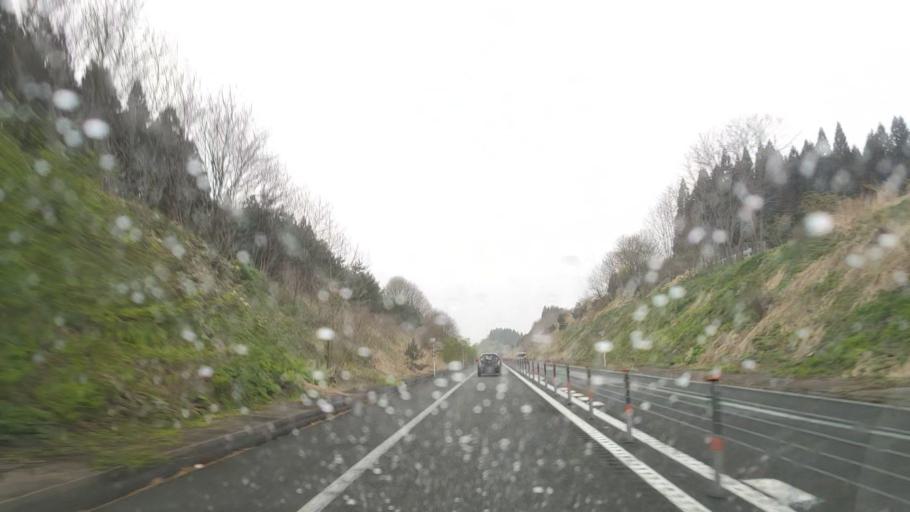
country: JP
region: Akita
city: Noshiromachi
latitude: 40.2011
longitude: 140.1445
